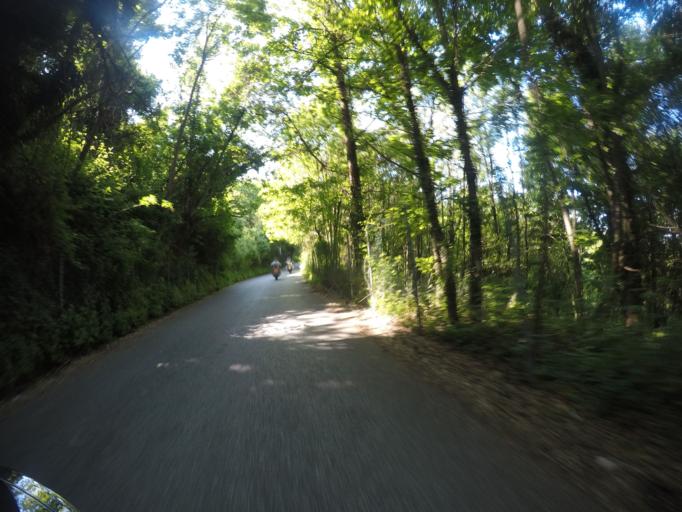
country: IT
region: Tuscany
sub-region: Provincia di Massa-Carrara
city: Montignoso
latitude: 44.0512
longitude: 10.1694
